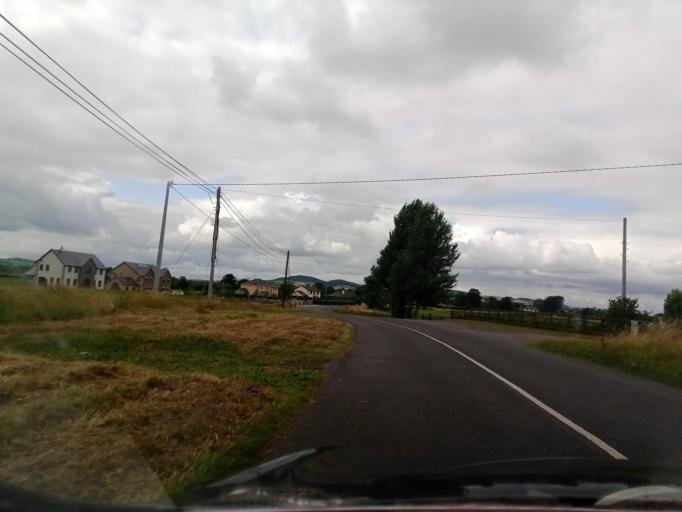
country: IE
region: Leinster
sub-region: Laois
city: Stradbally
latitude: 52.9774
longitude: -7.1799
